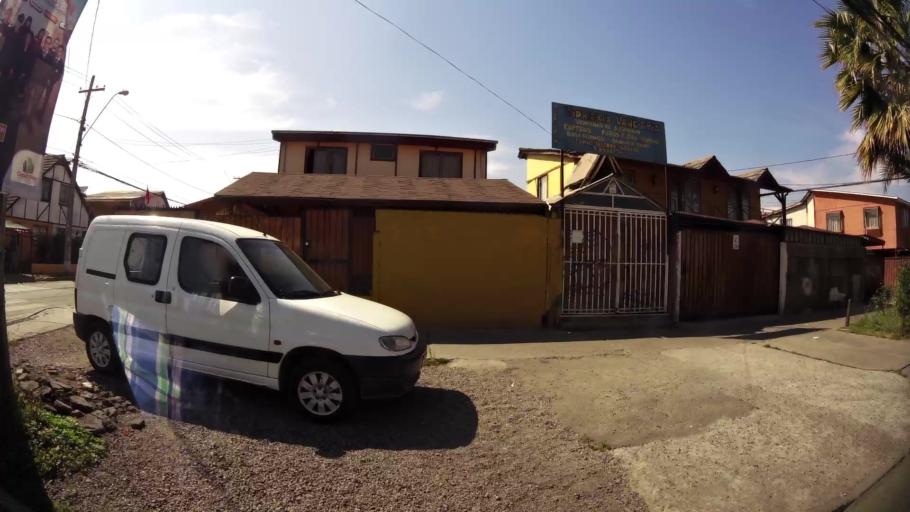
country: CL
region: Santiago Metropolitan
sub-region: Provincia de Santiago
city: Lo Prado
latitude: -33.4718
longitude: -70.7483
